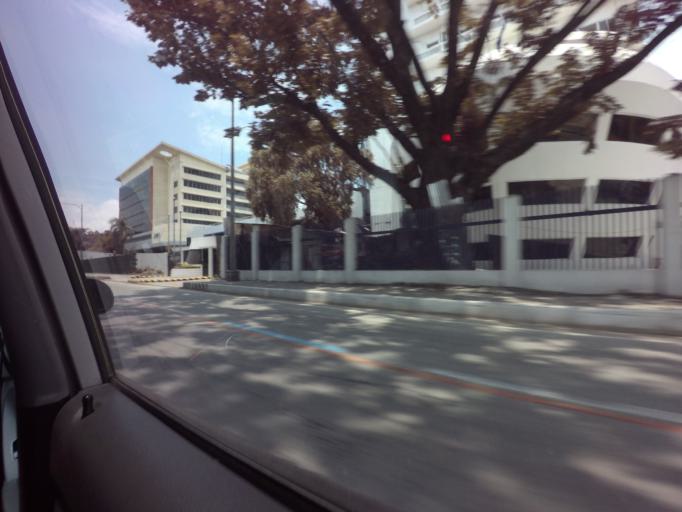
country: PH
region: Metro Manila
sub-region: City of Manila
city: Port Area
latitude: 14.5871
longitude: 120.9730
